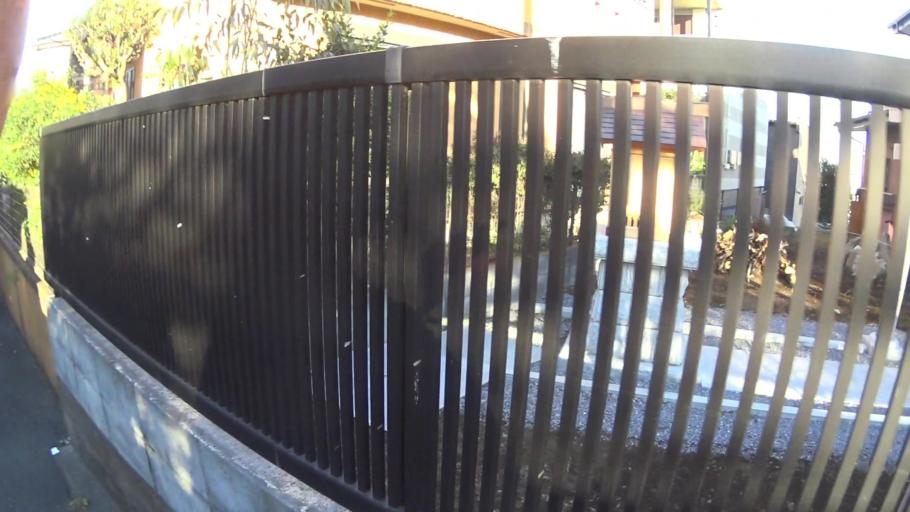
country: JP
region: Saitama
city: Shimotoda
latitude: 35.8493
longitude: 139.6903
